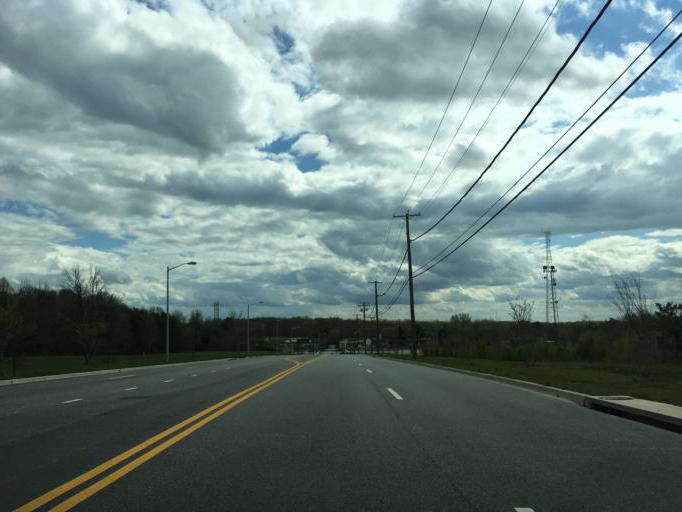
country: US
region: Maryland
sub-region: Anne Arundel County
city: Jessup
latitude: 39.1408
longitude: -76.7516
